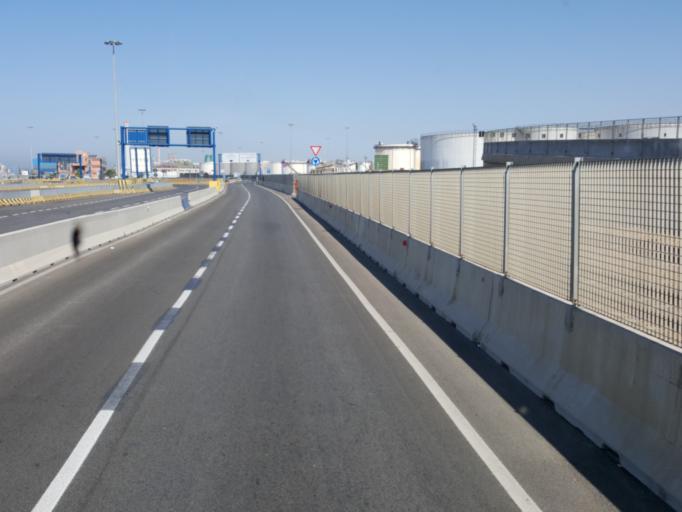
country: IT
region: Latium
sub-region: Citta metropolitana di Roma Capitale
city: Civitavecchia
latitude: 42.1016
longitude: 11.7829
